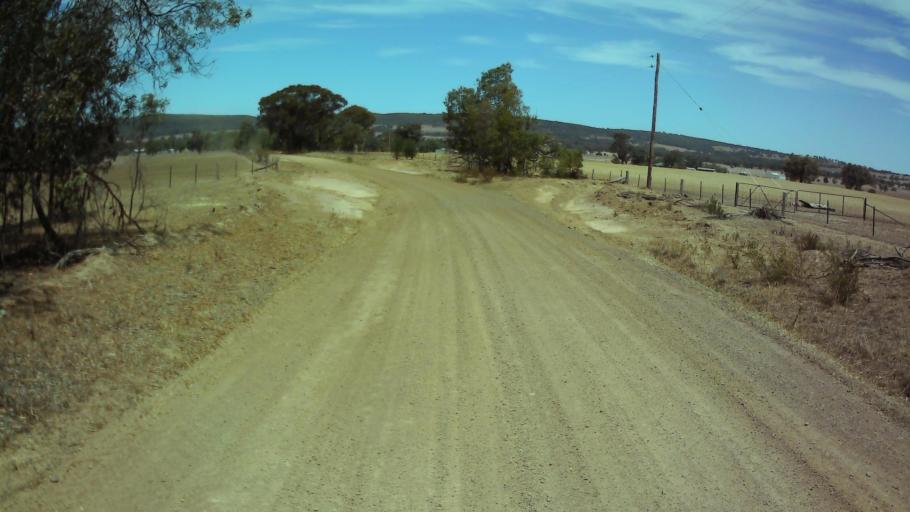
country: AU
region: New South Wales
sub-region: Weddin
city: Grenfell
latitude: -33.8261
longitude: 148.1710
